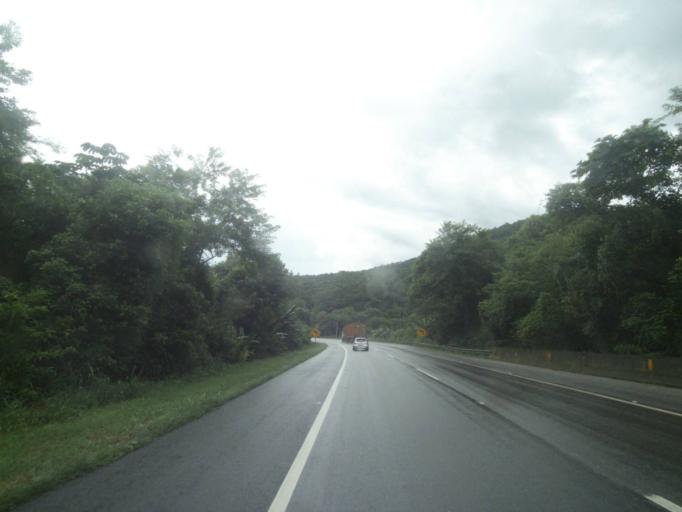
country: BR
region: Parana
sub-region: Antonina
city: Antonina
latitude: -25.5610
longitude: -48.8158
